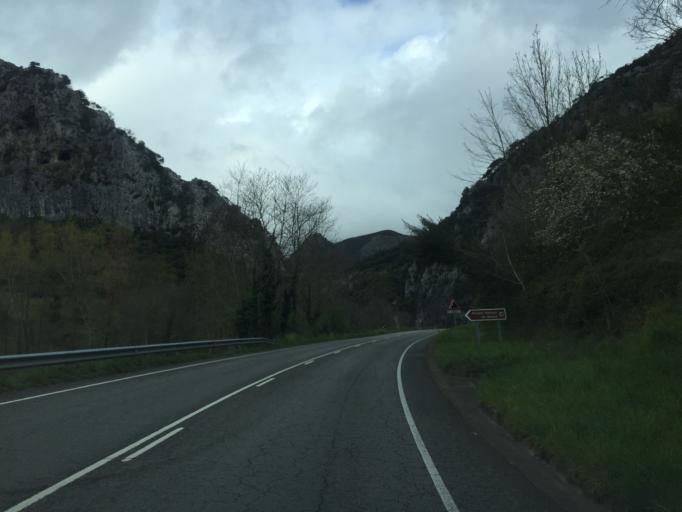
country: ES
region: Asturias
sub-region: Province of Asturias
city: Carrena
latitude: 43.3106
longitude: -4.8376
